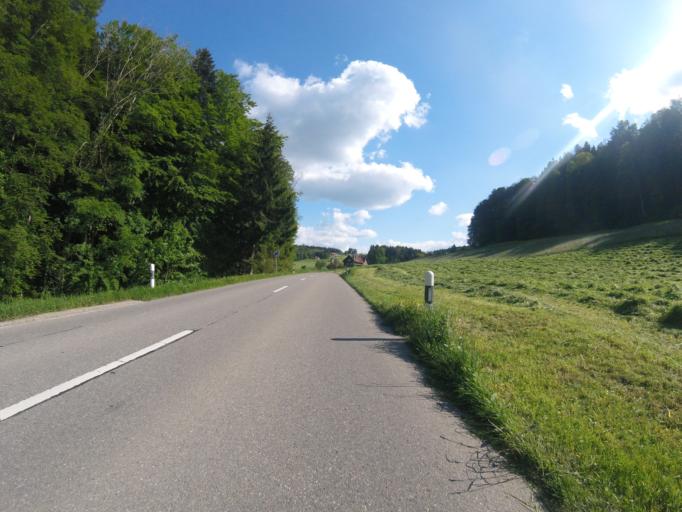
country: CH
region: Saint Gallen
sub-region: Wahlkreis Wil
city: Degersheim
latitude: 47.3899
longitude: 9.1936
